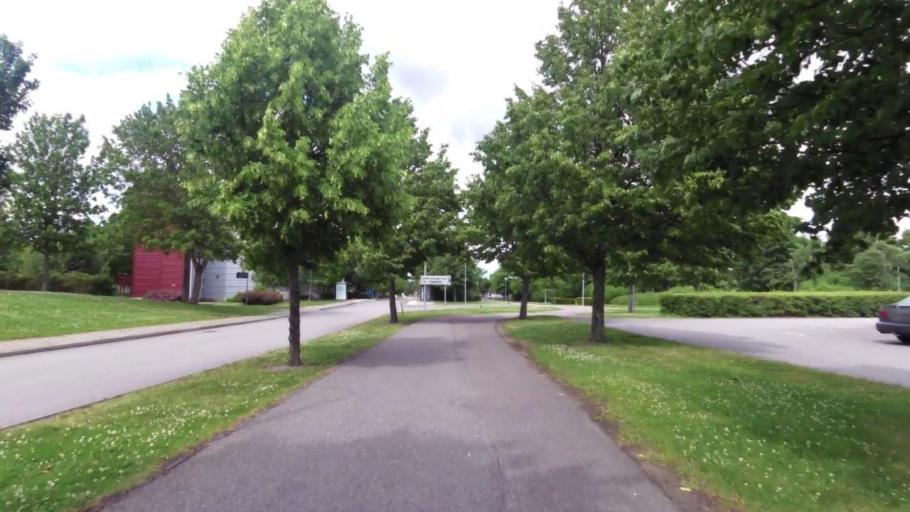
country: SE
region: OEstergoetland
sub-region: Linkopings Kommun
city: Linkoping
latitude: 58.3941
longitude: 15.5733
